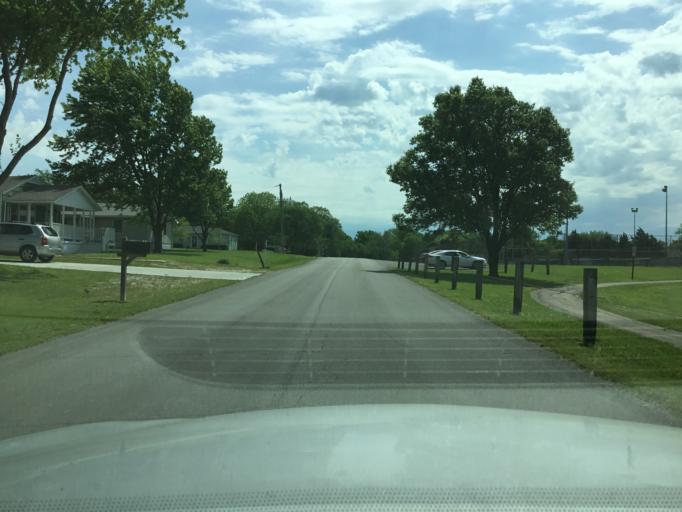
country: US
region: Kansas
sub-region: Montgomery County
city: Coffeyville
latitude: 37.0544
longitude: -95.6415
